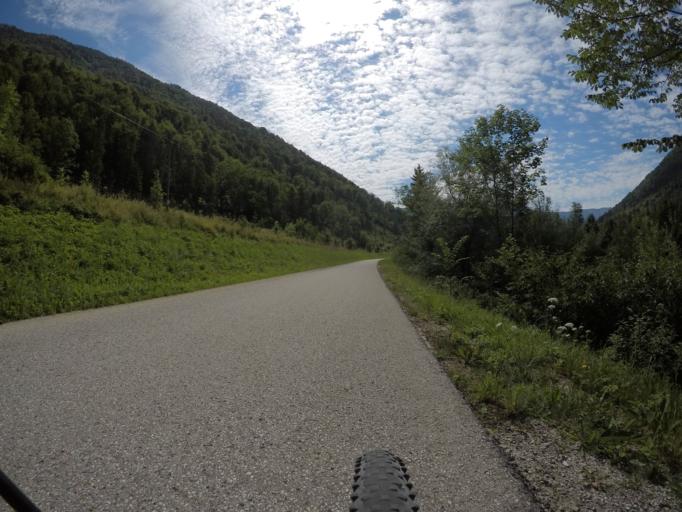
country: AT
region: Lower Austria
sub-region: Politischer Bezirk Amstetten
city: Hollenstein an der Ybbs
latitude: 47.8170
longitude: 14.7621
